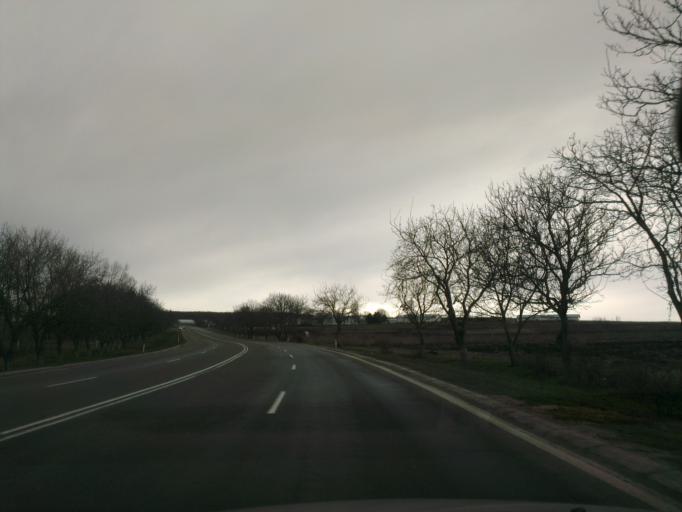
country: MD
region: Laloveni
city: Ialoveni
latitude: 46.9506
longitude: 28.7242
